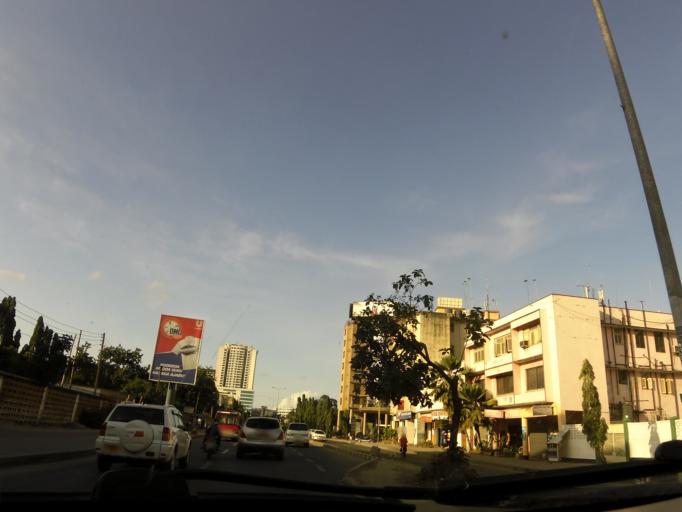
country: TZ
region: Dar es Salaam
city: Dar es Salaam
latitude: -6.8148
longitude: 39.2817
